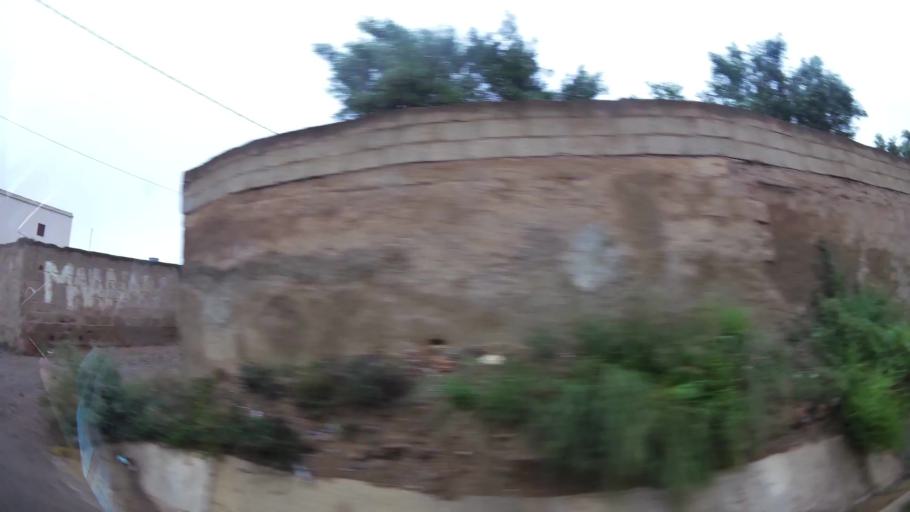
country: MA
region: Oriental
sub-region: Nador
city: Boudinar
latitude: 35.1314
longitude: -3.5894
